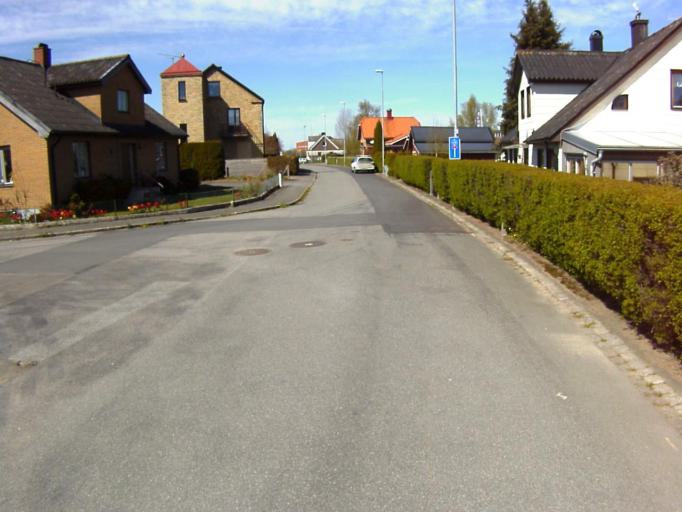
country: SE
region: Skane
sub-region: Kristianstads Kommun
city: Kristianstad
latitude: 56.0107
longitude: 14.1541
